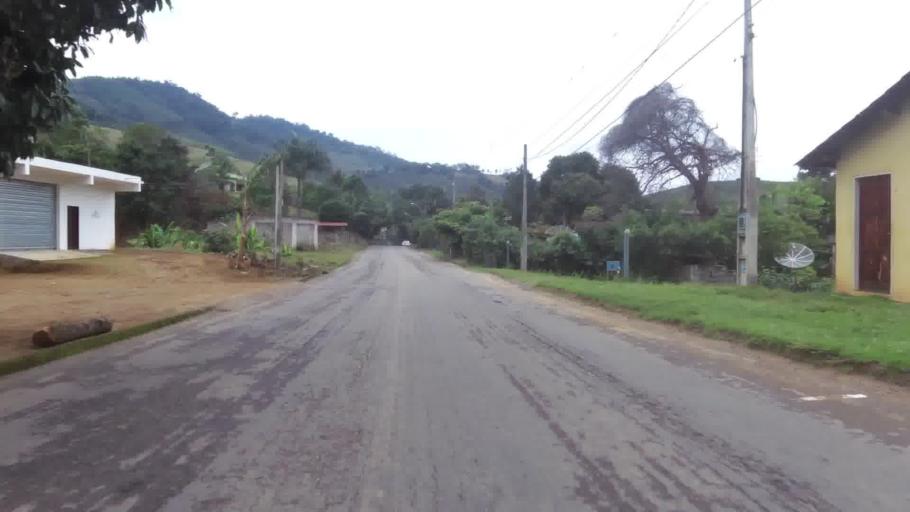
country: BR
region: Espirito Santo
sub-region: Iconha
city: Iconha
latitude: -20.7793
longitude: -40.8263
